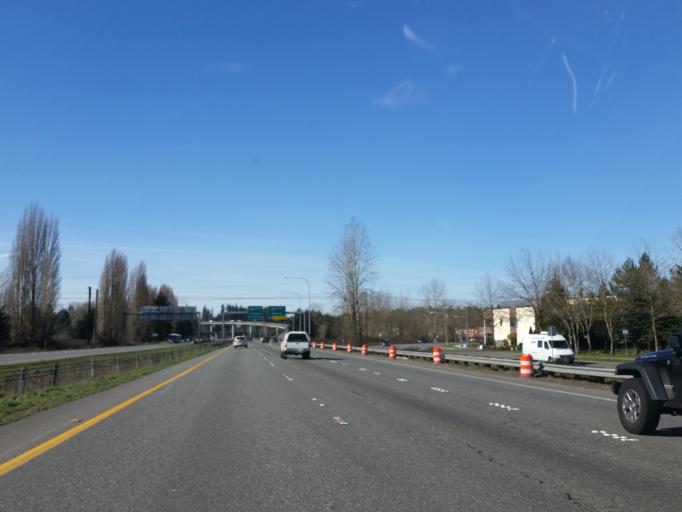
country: US
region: Washington
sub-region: King County
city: Woodinville
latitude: 47.7577
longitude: -122.1707
